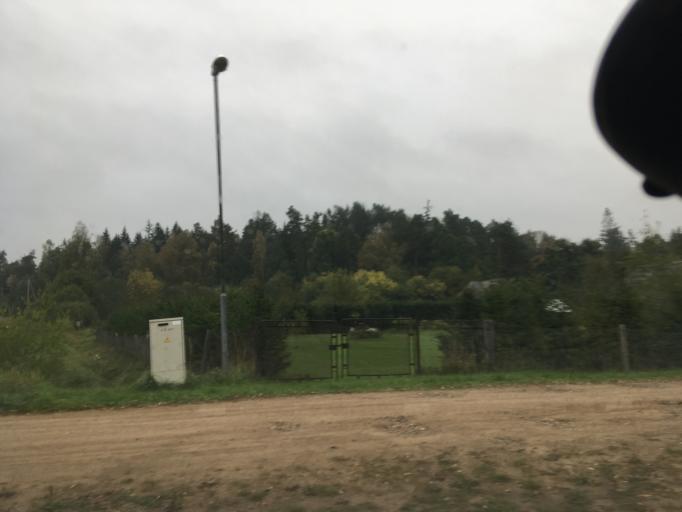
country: LV
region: Kuldigas Rajons
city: Kuldiga
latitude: 56.9862
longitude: 22.0168
